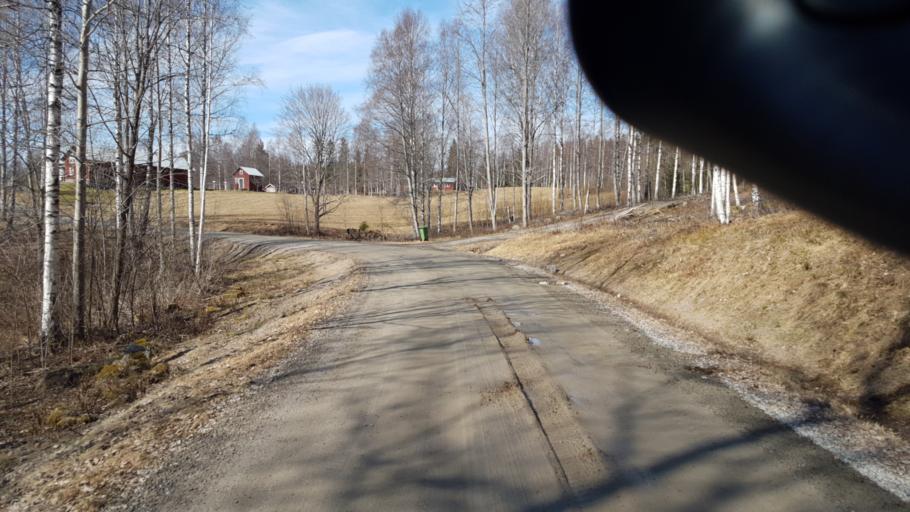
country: SE
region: Vaermland
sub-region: Arvika Kommun
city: Arvika
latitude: 59.7151
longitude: 12.8462
